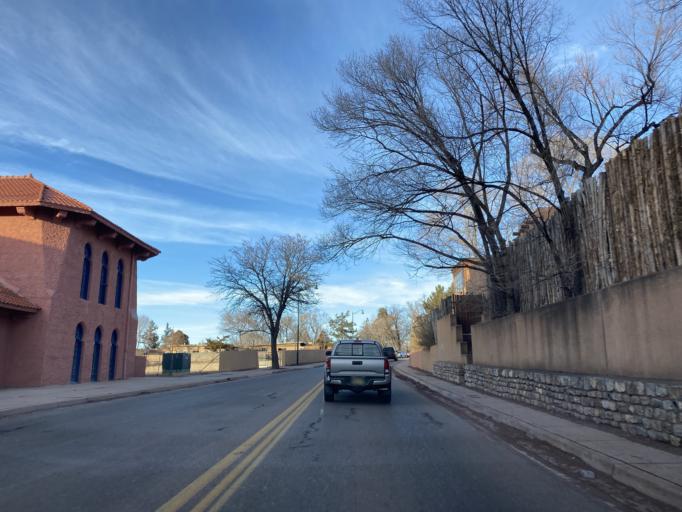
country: US
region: New Mexico
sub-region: Santa Fe County
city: Santa Fe
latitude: 35.6916
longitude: -105.9361
